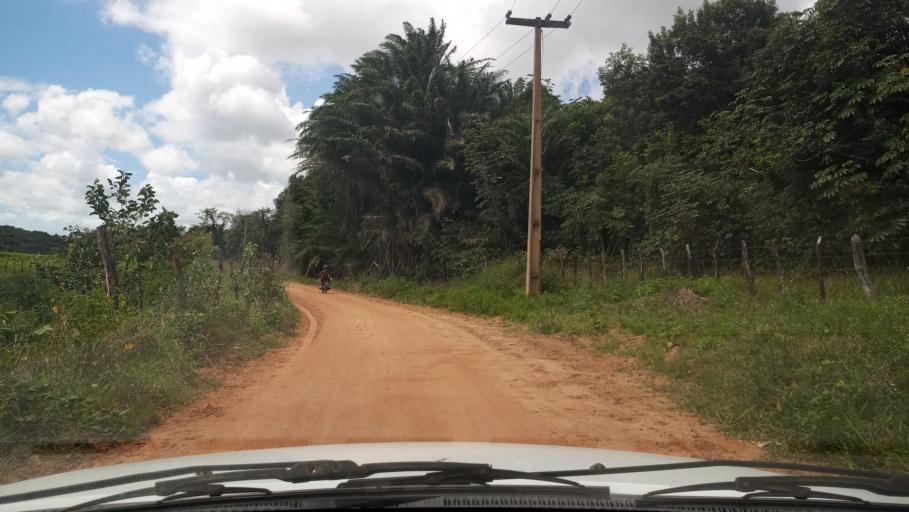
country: BR
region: Rio Grande do Norte
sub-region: Goianinha
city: Goianinha
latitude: -6.2605
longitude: -35.2484
